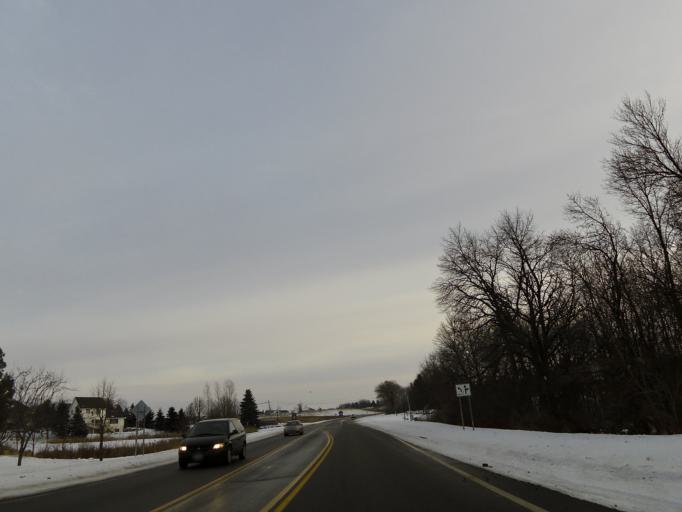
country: US
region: Minnesota
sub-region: Carver County
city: Victoria
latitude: 44.8498
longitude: -93.6580
